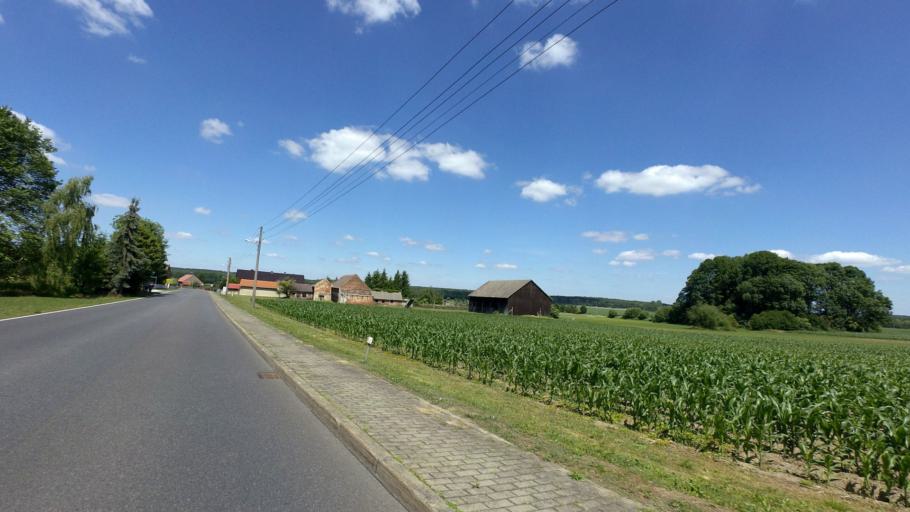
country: DE
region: Brandenburg
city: Kasel-Golzig
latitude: 51.8983
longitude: 13.6800
